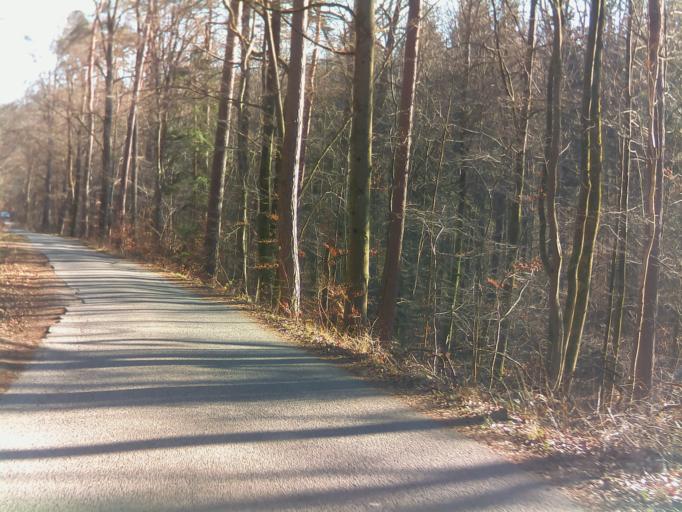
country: DE
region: Baden-Wuerttemberg
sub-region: Regierungsbezirk Stuttgart
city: Steinenbronn
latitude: 48.7067
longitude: 9.1012
